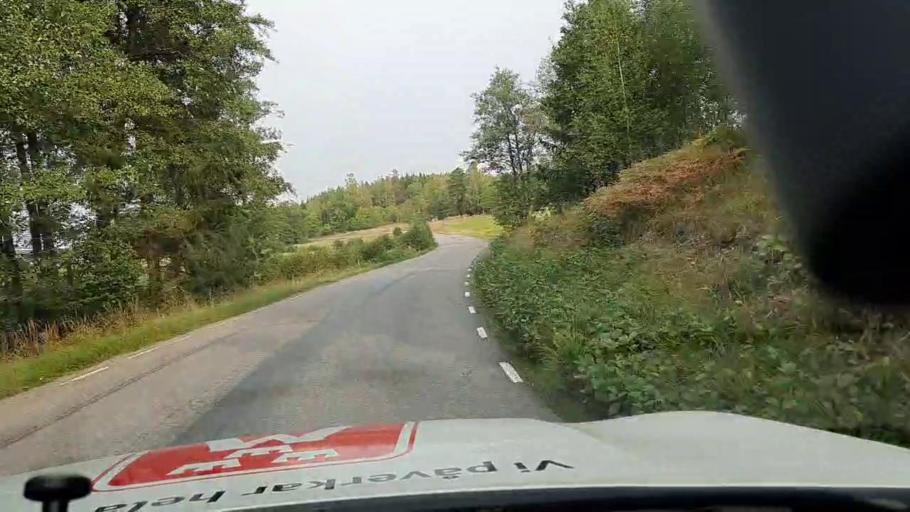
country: SE
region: Soedermanland
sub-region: Nykopings Kommun
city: Stigtomta
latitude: 58.9697
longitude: 16.9014
